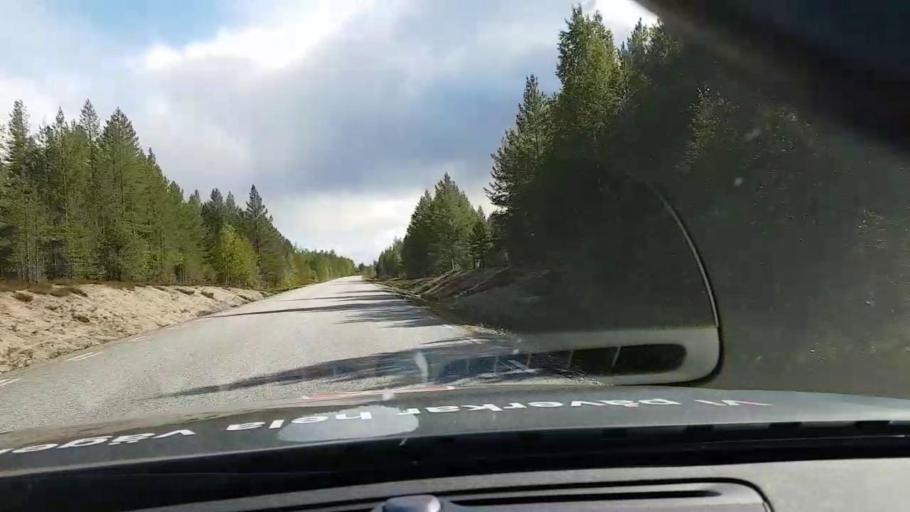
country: SE
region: Vaesterbotten
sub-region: Asele Kommun
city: Asele
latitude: 63.9115
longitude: 17.3366
